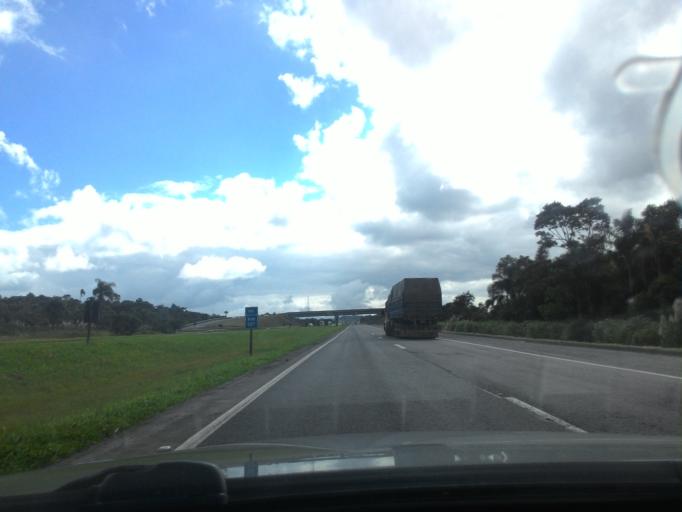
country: BR
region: Sao Paulo
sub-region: Cajati
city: Cajati
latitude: -24.9327
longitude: -48.2823
